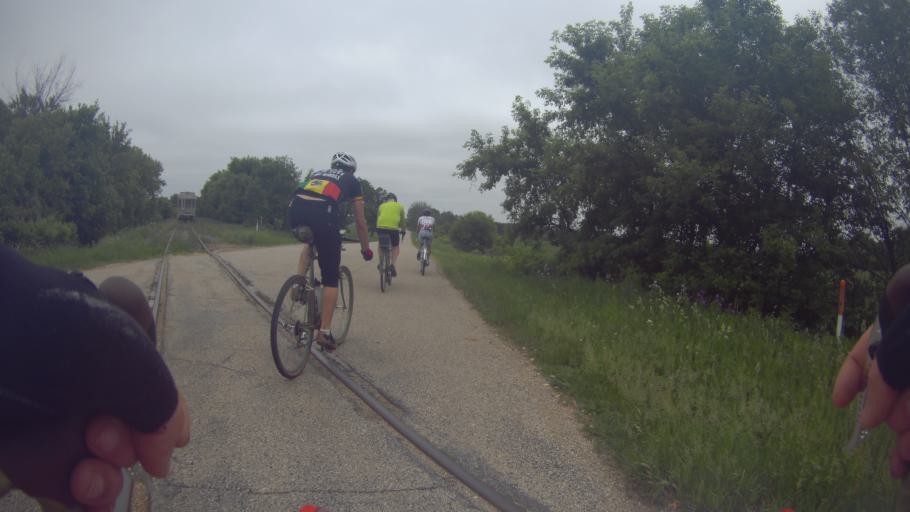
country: US
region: Wisconsin
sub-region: Green County
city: Brooklyn
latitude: 42.8864
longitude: -89.3885
